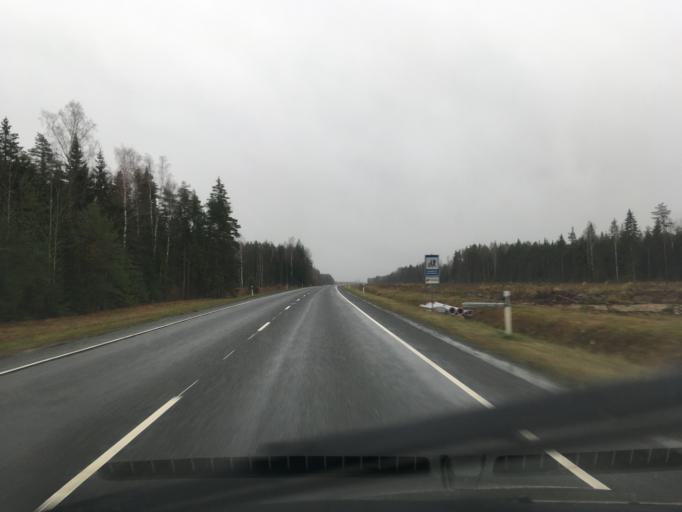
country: EE
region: Harju
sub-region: Nissi vald
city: Turba
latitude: 58.9666
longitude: 24.0685
